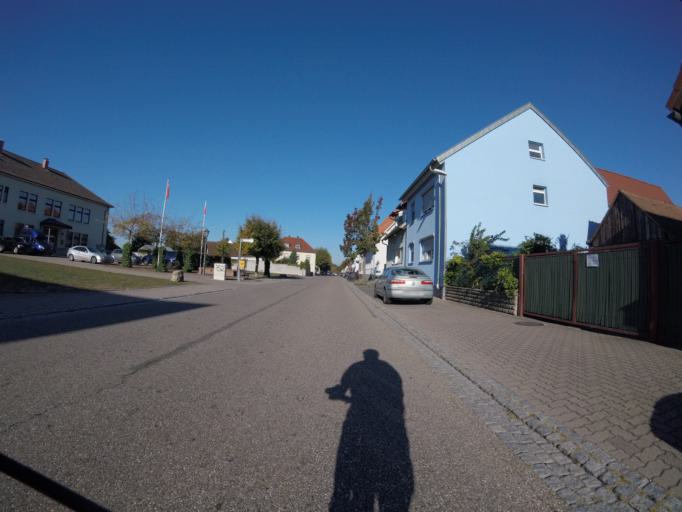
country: DE
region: Baden-Wuerttemberg
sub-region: Karlsruhe Region
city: Eggenstein-Leopoldshafen
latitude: 49.0996
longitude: 8.3919
